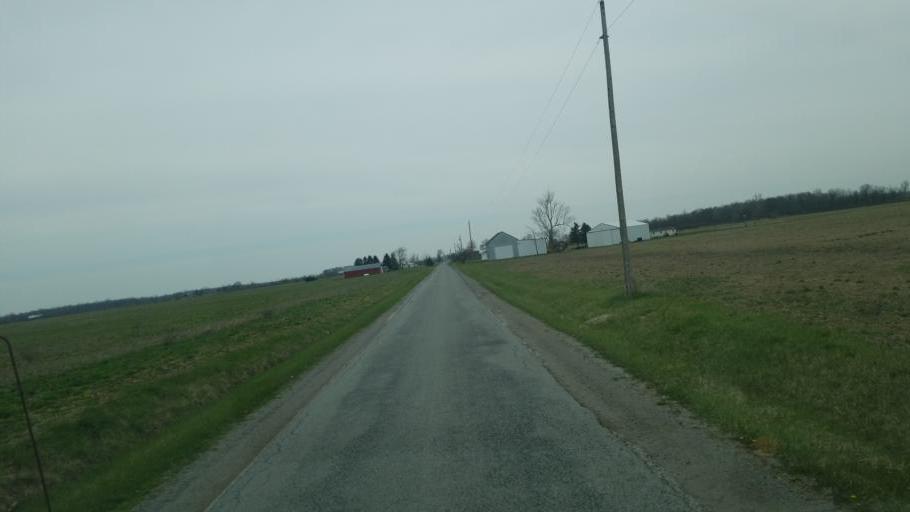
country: US
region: Ohio
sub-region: Hardin County
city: Forest
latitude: 40.8924
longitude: -83.5149
